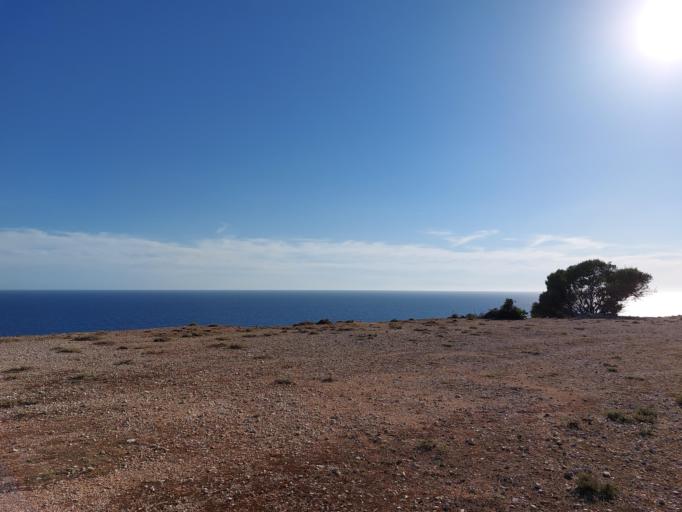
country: HR
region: Dubrovacko-Neretvanska
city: Smokvica
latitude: 42.7273
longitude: 16.8410
